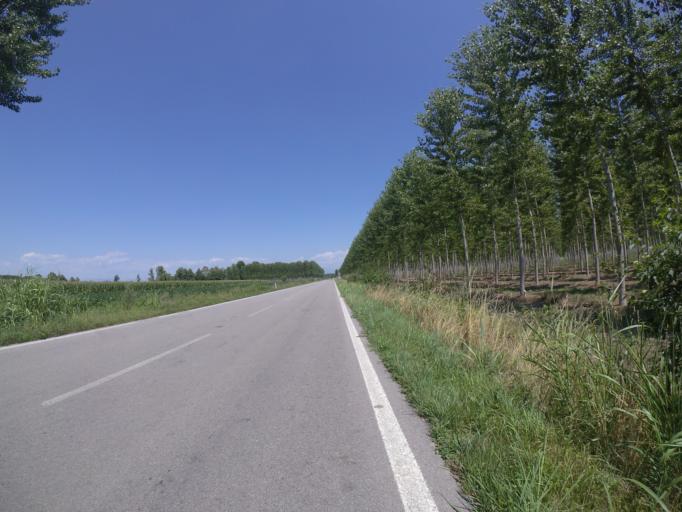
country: IT
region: Friuli Venezia Giulia
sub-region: Provincia di Udine
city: Talmassons
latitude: 45.8967
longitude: 13.1316
